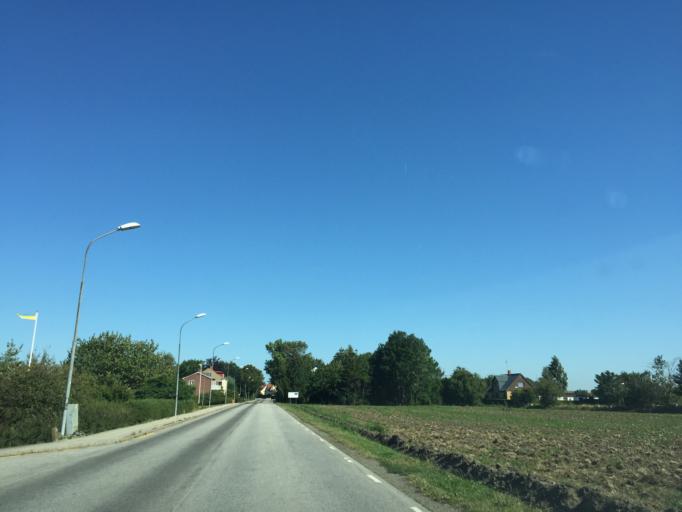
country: SE
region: Skane
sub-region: Ystads Kommun
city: Kopingebro
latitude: 55.4337
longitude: 14.1134
